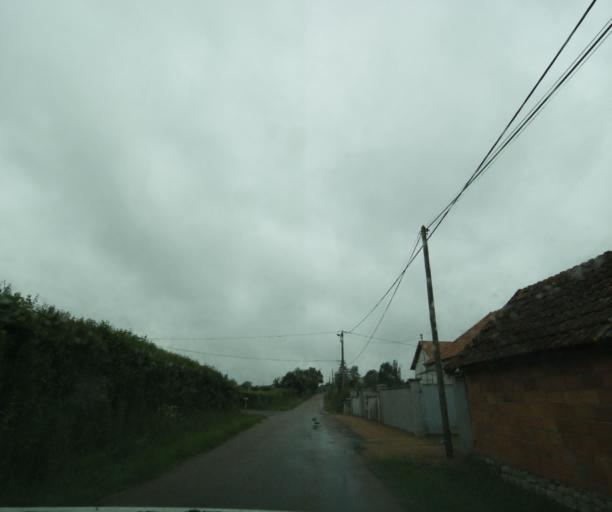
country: FR
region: Bourgogne
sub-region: Departement de Saone-et-Loire
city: Palinges
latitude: 46.5465
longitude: 4.1947
